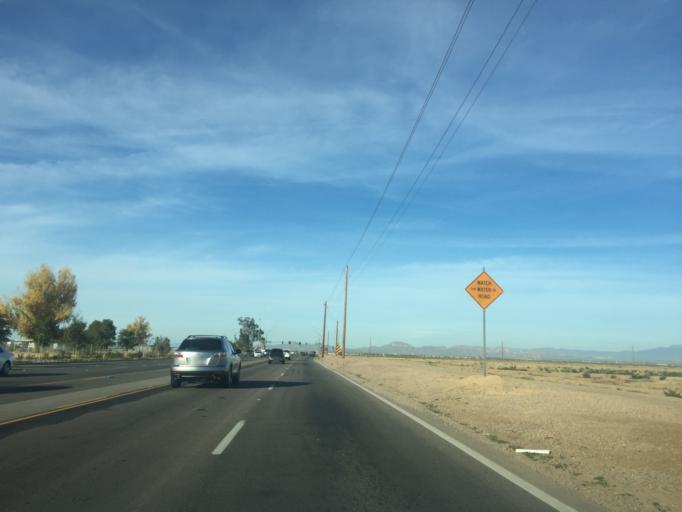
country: US
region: Arizona
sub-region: Maricopa County
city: Queen Creek
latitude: 33.2749
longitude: -111.6348
